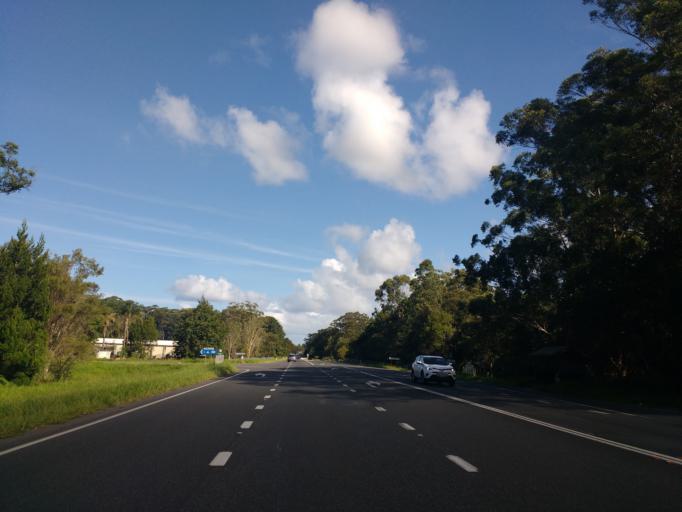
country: AU
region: New South Wales
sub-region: Ballina
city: Ballina
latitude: -28.9213
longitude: 153.4763
